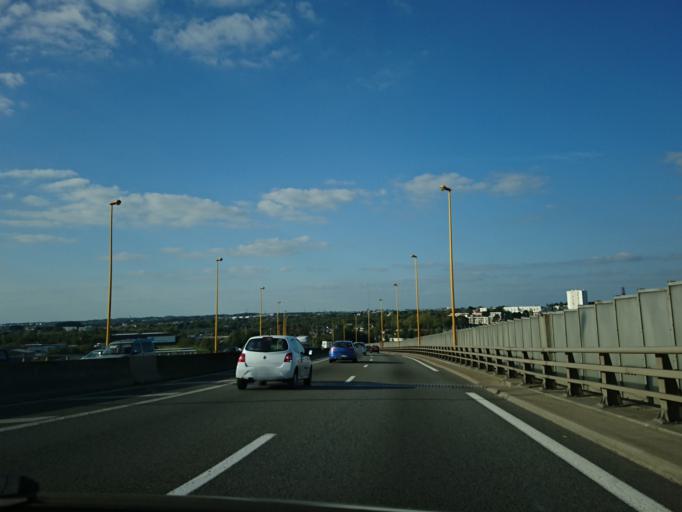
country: FR
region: Pays de la Loire
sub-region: Departement de la Loire-Atlantique
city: Bouguenais
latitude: 47.1966
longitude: -1.6158
